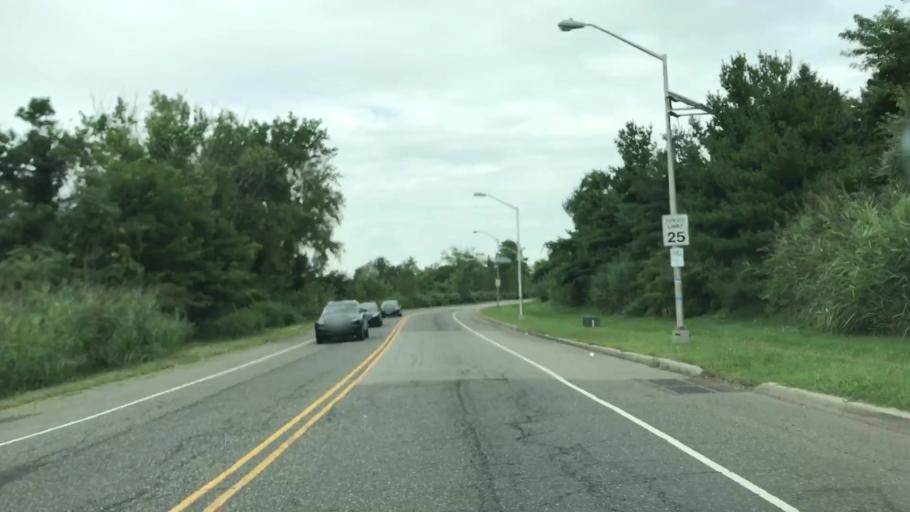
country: US
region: New Jersey
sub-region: Hudson County
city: Jersey City
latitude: 40.6966
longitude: -74.0763
